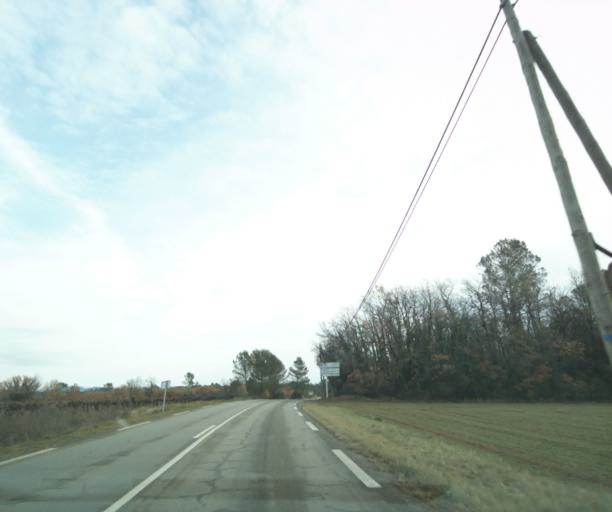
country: FR
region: Provence-Alpes-Cote d'Azur
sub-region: Departement du Var
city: Rougiers
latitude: 43.3982
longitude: 5.8818
